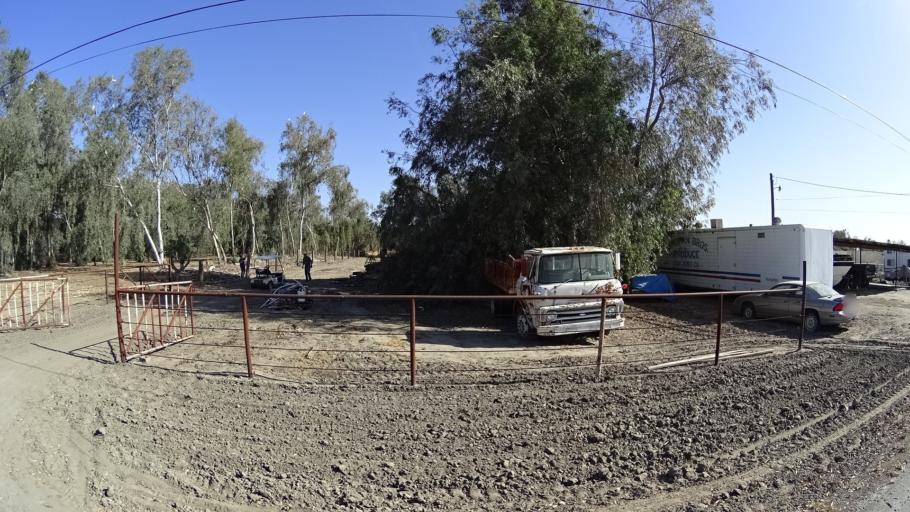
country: US
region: California
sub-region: Kings County
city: Corcoran
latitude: 36.0944
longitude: -119.5936
